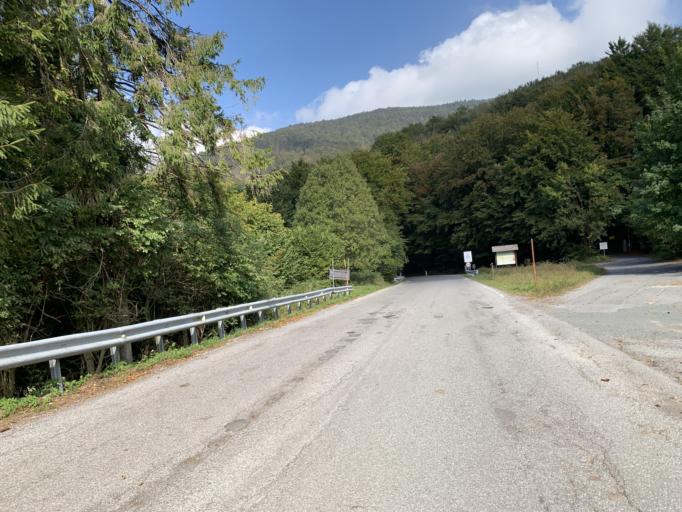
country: IT
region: Liguria
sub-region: Provincia di Savona
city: Osiglia
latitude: 44.2309
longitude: 8.1968
